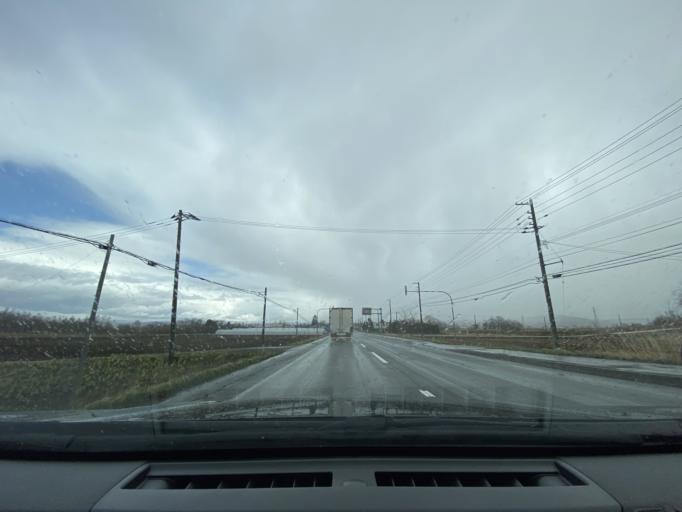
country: JP
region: Hokkaido
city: Fukagawa
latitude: 43.6779
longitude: 142.0312
